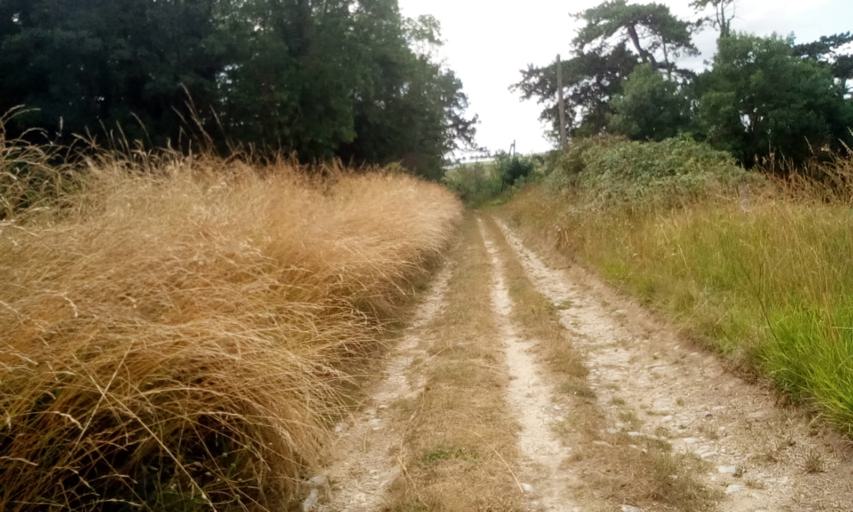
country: FR
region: Lower Normandy
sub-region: Departement du Calvados
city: Creully
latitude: 49.2885
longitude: -0.5196
